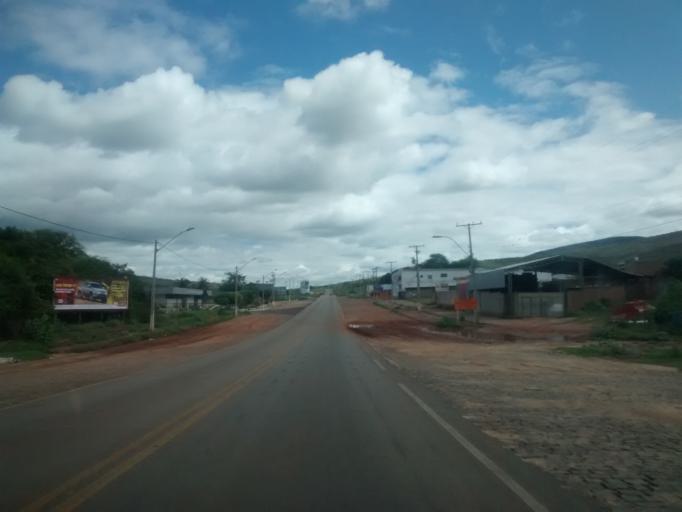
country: BR
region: Bahia
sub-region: Brumado
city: Brumado
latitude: -14.2184
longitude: -41.6860
